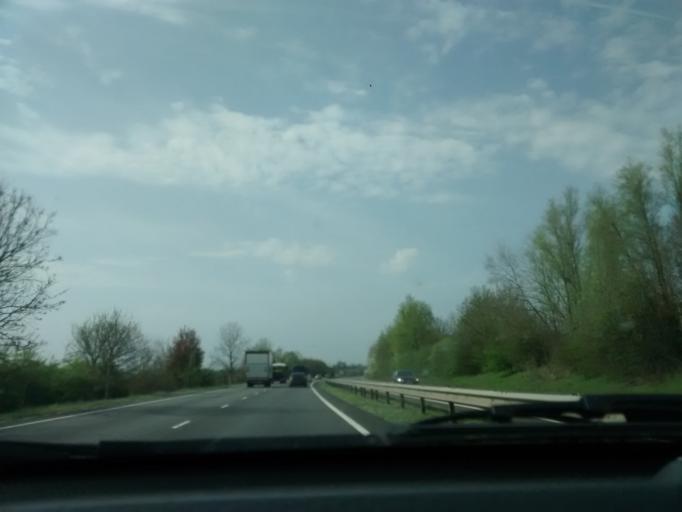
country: GB
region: England
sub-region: Oxfordshire
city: Kidlington
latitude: 51.8151
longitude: -1.2653
